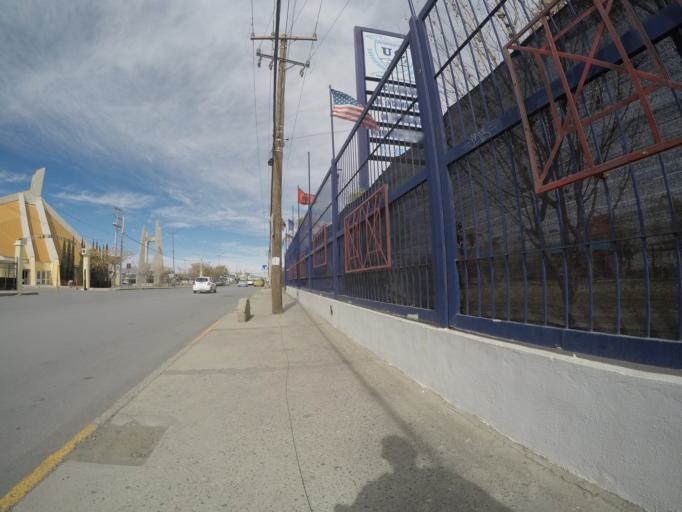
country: MX
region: Chihuahua
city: Ciudad Juarez
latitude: 31.7198
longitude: -106.4316
